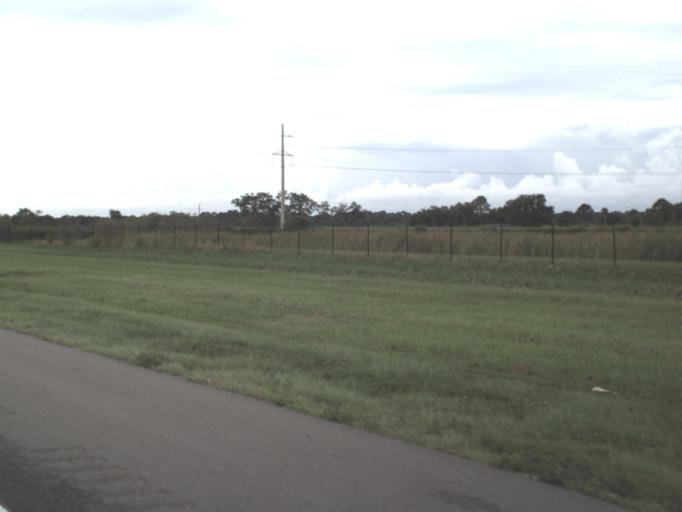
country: US
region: Florida
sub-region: Sarasota County
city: Laurel
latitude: 27.1783
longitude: -82.4360
